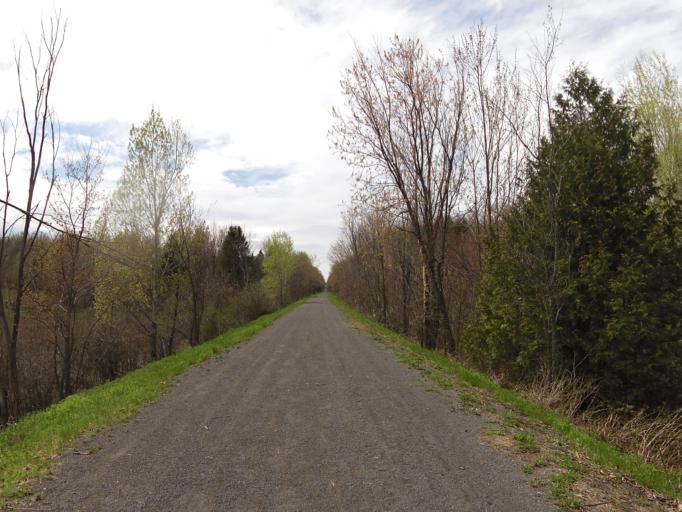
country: CA
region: Ontario
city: Hawkesbury
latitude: 45.5325
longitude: -74.6855
